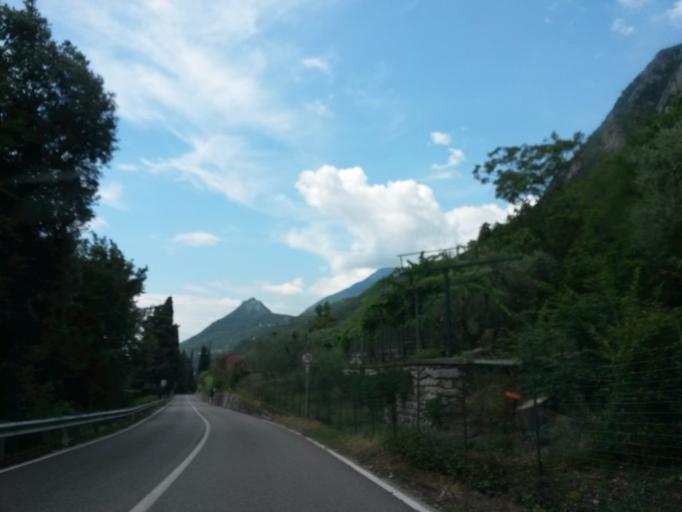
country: IT
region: Lombardy
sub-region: Provincia di Brescia
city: Gargnano
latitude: 45.6993
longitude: 10.6761
